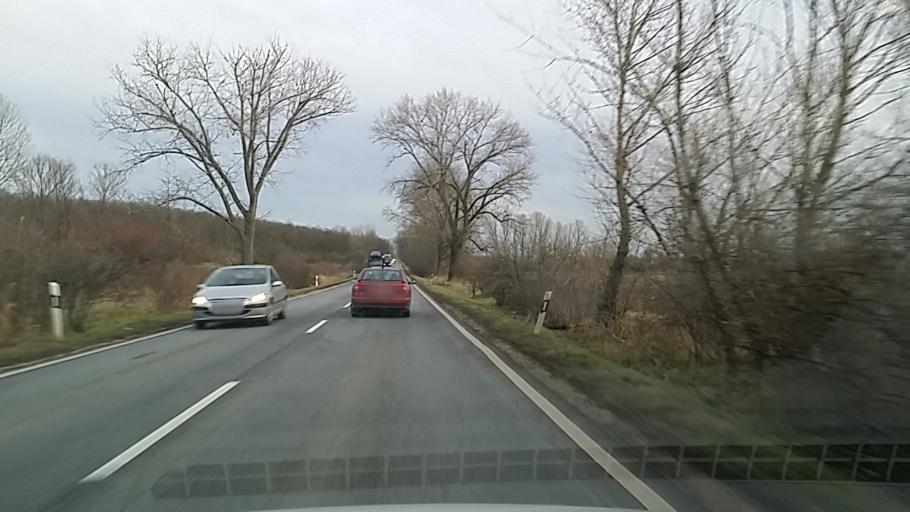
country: HU
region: Fejer
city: Mor
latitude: 47.3557
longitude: 18.2136
